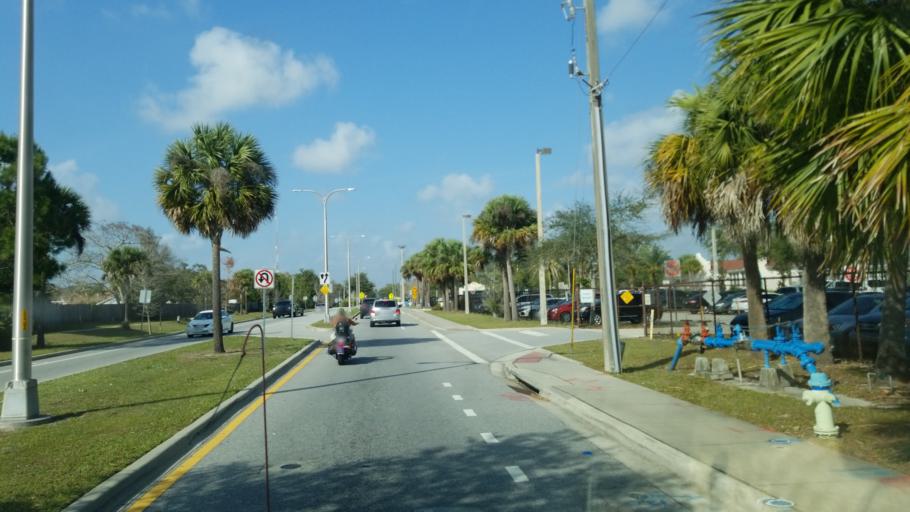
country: US
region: Florida
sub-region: Sarasota County
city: Fruitville
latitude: 27.3307
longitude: -82.4638
